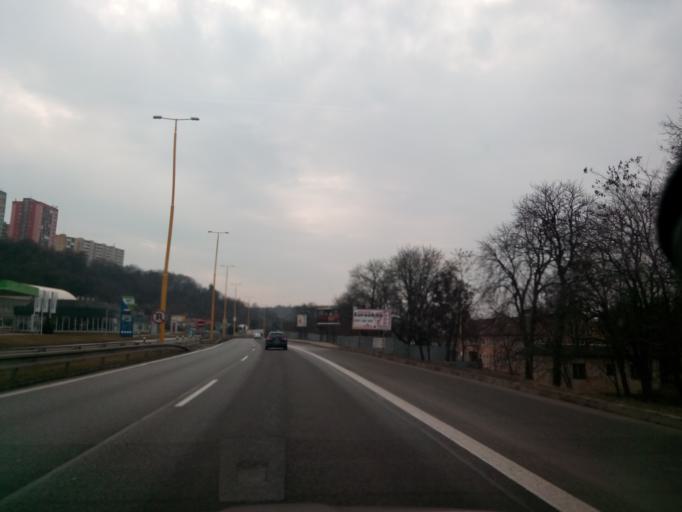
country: SK
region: Kosicky
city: Kosice
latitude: 48.7344
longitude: 21.2745
